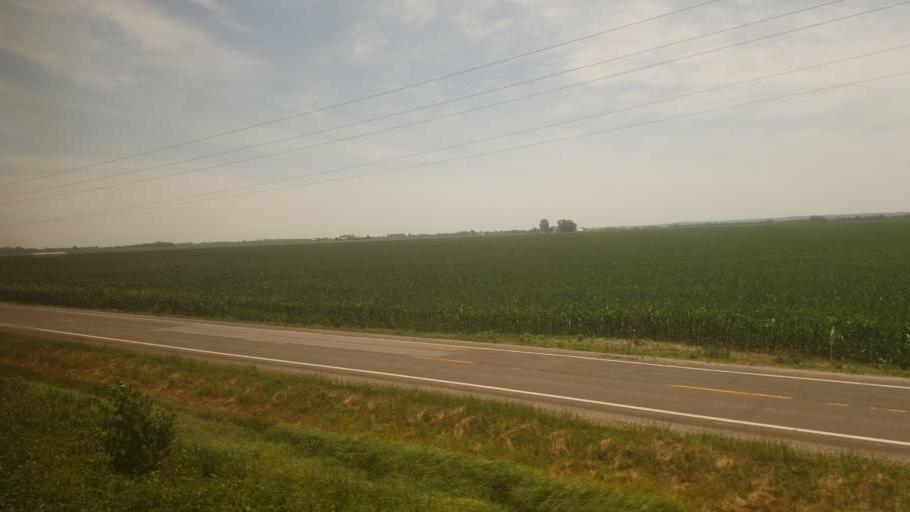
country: US
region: Missouri
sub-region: Carroll County
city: Carrollton
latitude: 39.3069
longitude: -93.6615
